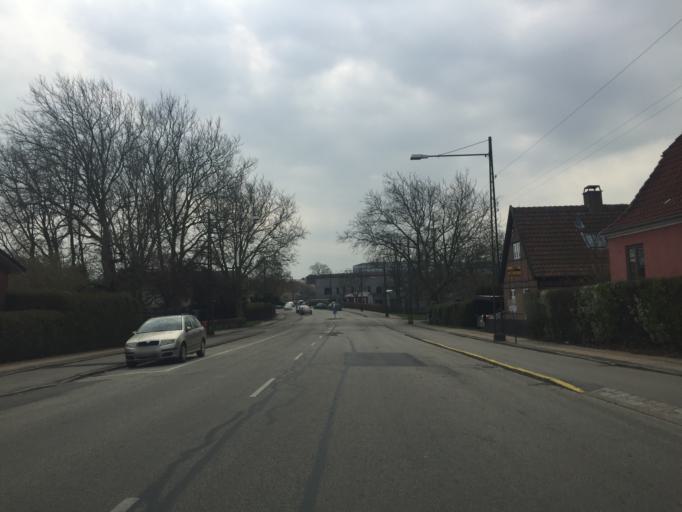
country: DK
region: Capital Region
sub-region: Kobenhavn
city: Vanlose
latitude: 55.7132
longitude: 12.5128
